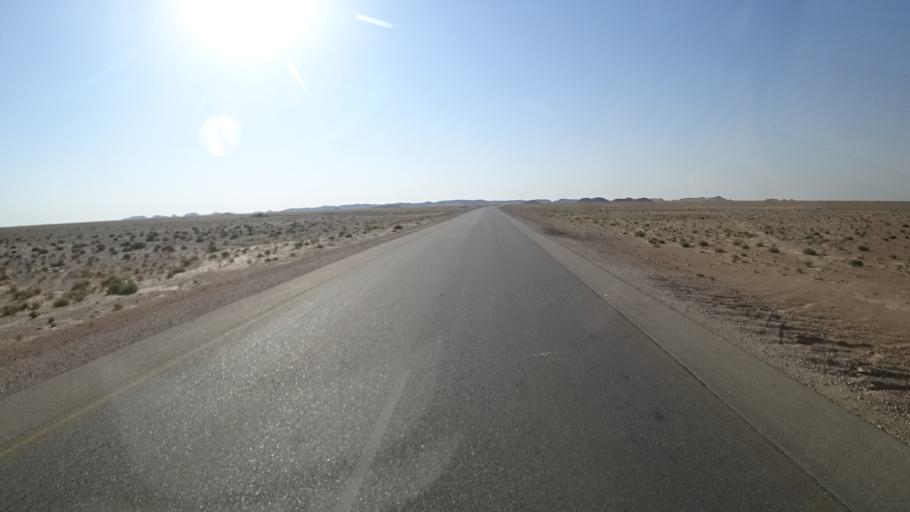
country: OM
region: Zufar
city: Salalah
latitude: 17.6390
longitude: 53.8878
